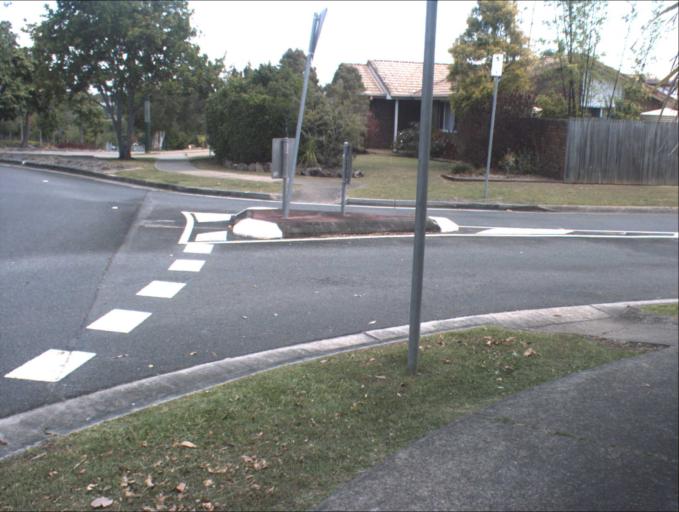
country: AU
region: Queensland
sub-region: Logan
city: Slacks Creek
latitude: -27.6367
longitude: 153.1476
